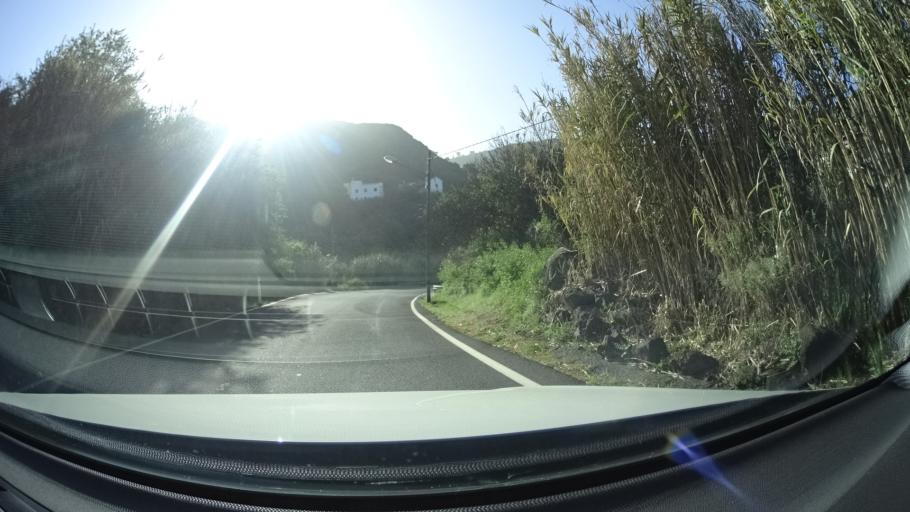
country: ES
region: Canary Islands
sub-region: Provincia de Las Palmas
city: Vega de San Mateo
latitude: 28.0168
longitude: -15.5538
